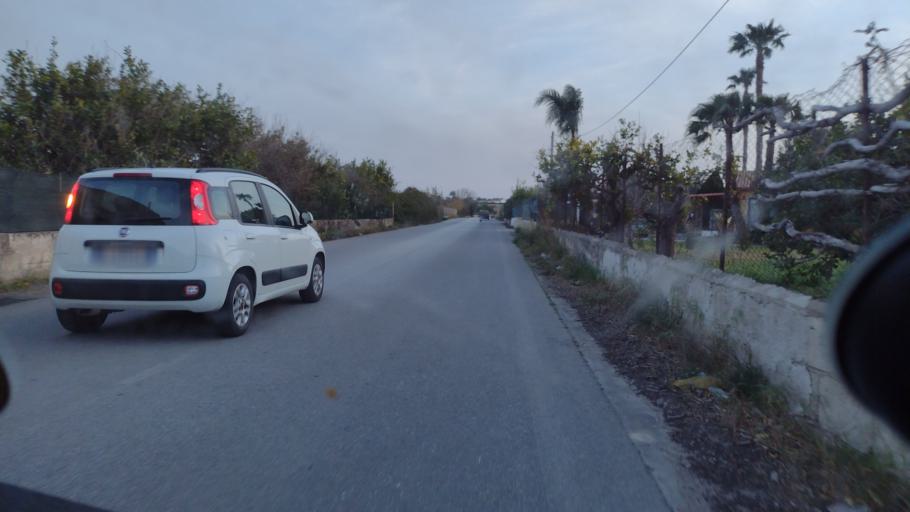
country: IT
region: Sicily
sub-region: Provincia di Siracusa
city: Avola
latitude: 36.8770
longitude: 15.1273
